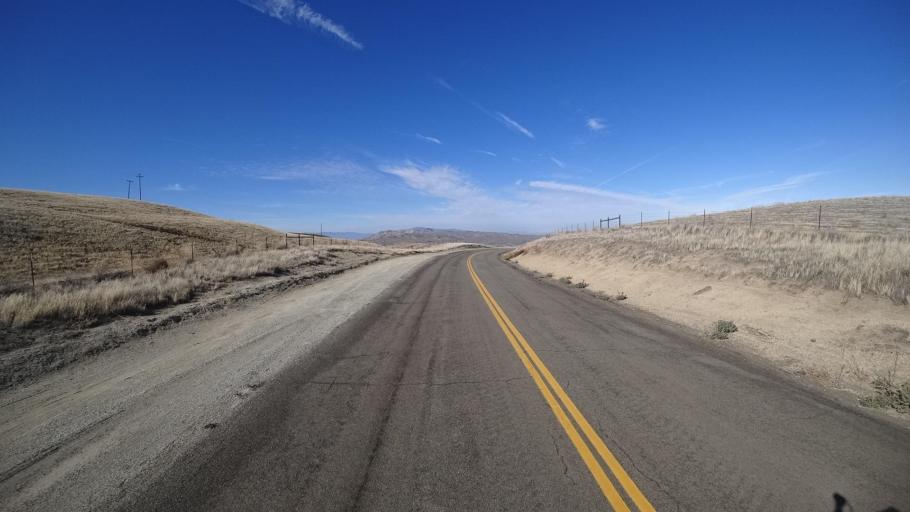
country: US
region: California
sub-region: Kern County
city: Maricopa
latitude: 34.9416
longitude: -119.4089
